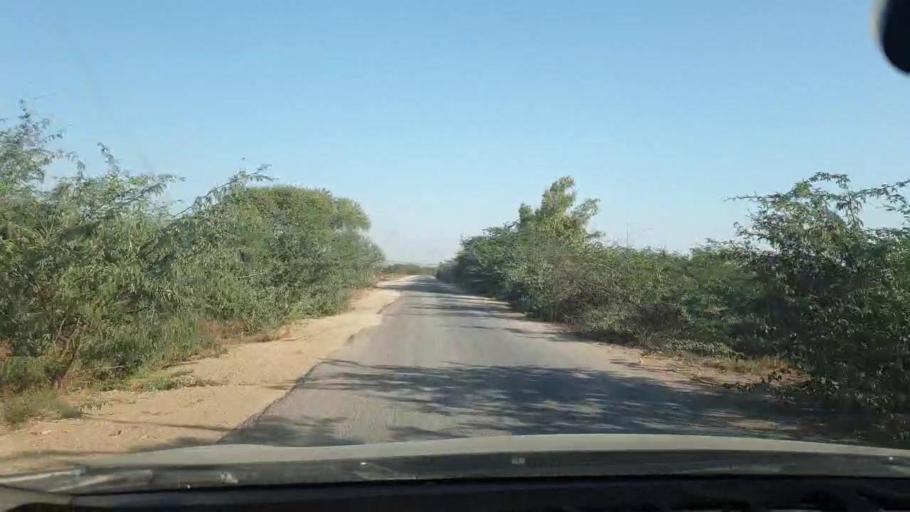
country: PK
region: Sindh
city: Malir Cantonment
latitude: 25.1534
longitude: 67.1906
